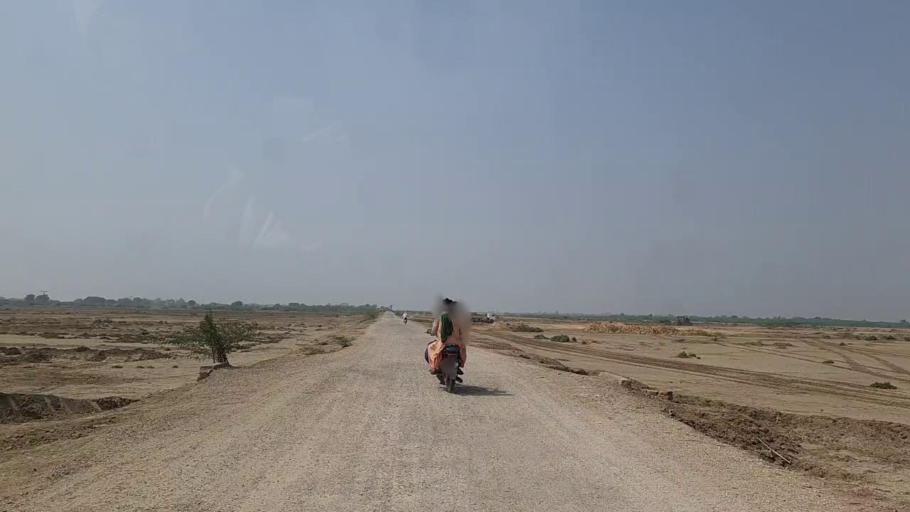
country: PK
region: Sindh
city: Naukot
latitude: 24.8299
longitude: 69.3908
